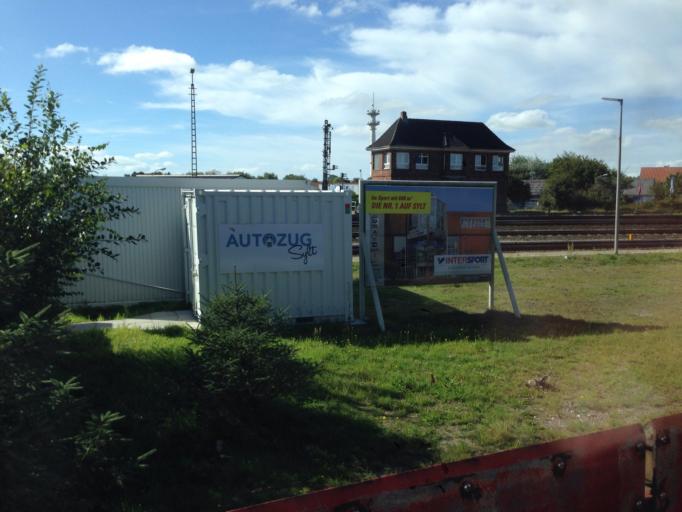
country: DE
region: Schleswig-Holstein
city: Niebull
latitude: 54.7851
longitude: 8.8359
